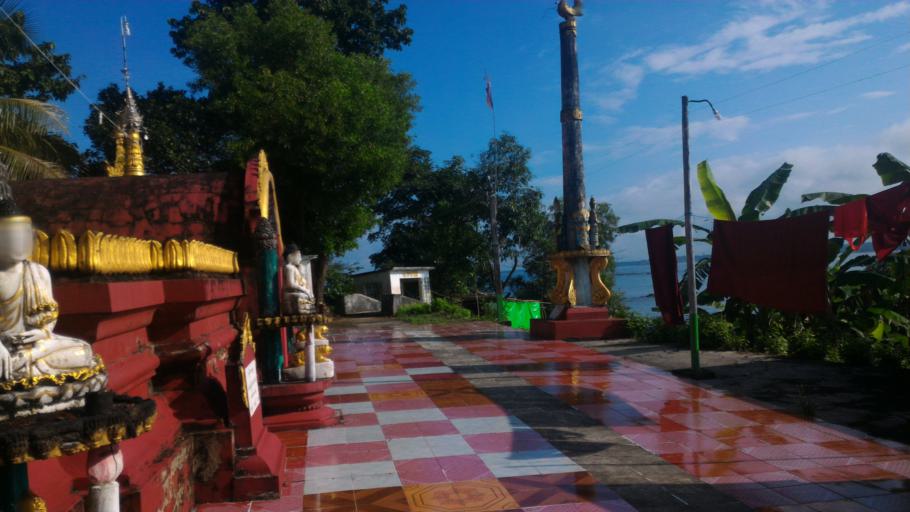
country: MM
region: Ayeyarwady
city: Pathein
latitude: 16.9562
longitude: 94.4284
